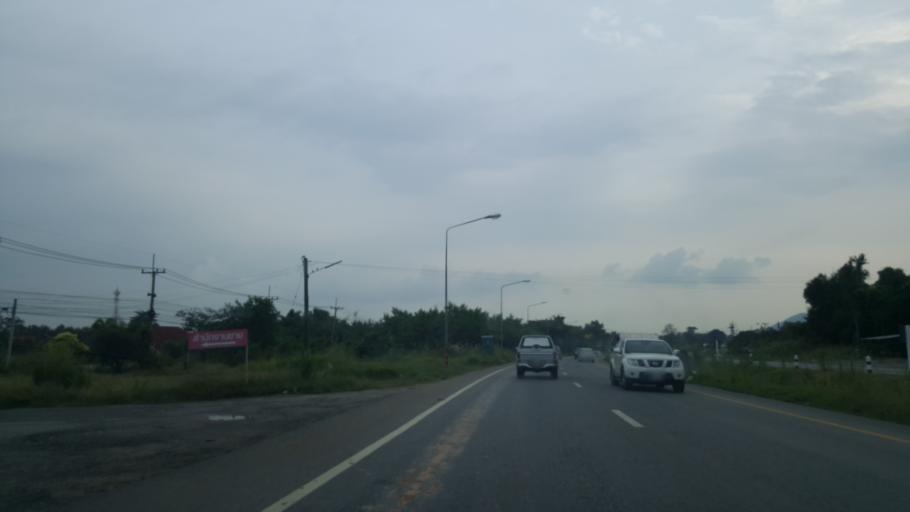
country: TH
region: Rayong
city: Ban Chang
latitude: 12.7406
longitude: 100.9906
